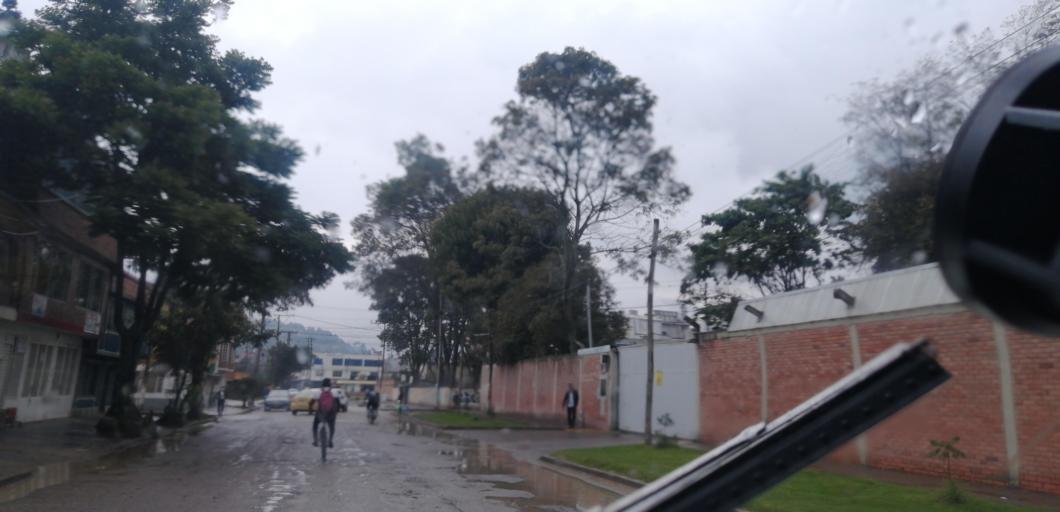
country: CO
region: Cundinamarca
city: Madrid
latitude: 4.7316
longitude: -74.2568
